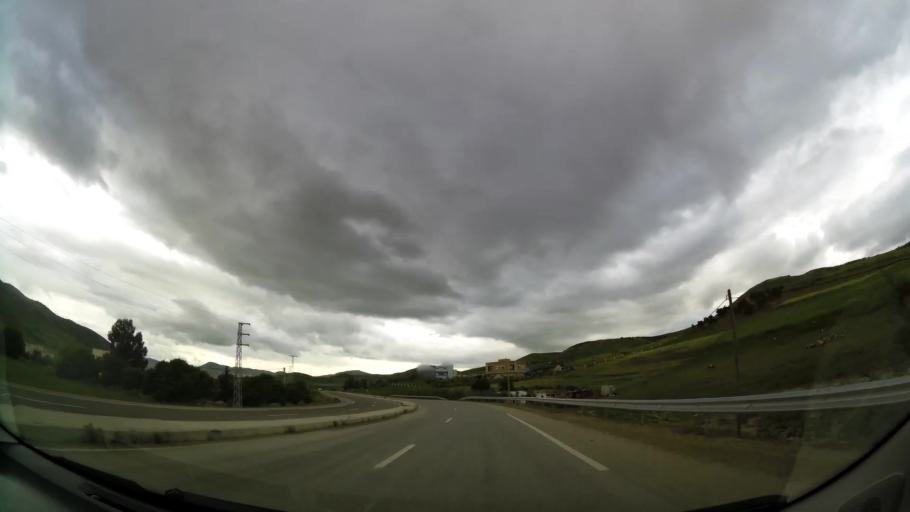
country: MA
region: Taza-Al Hoceima-Taounate
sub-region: Taza
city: Taza
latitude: 34.3400
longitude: -3.9356
